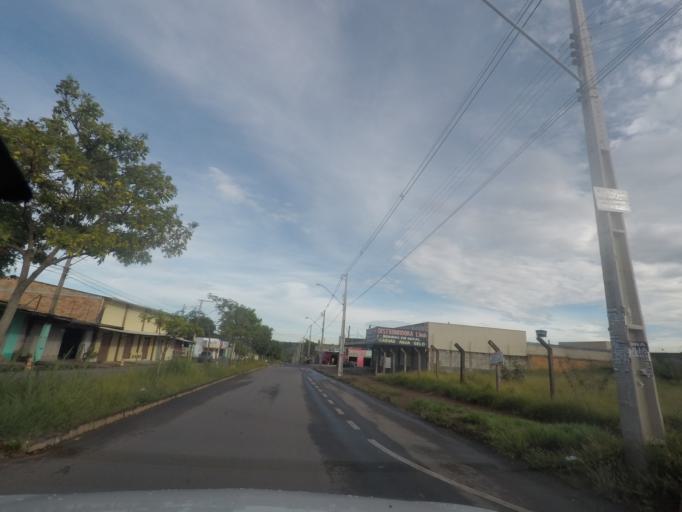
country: BR
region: Goias
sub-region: Aparecida De Goiania
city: Aparecida de Goiania
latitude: -16.7881
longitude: -49.3719
